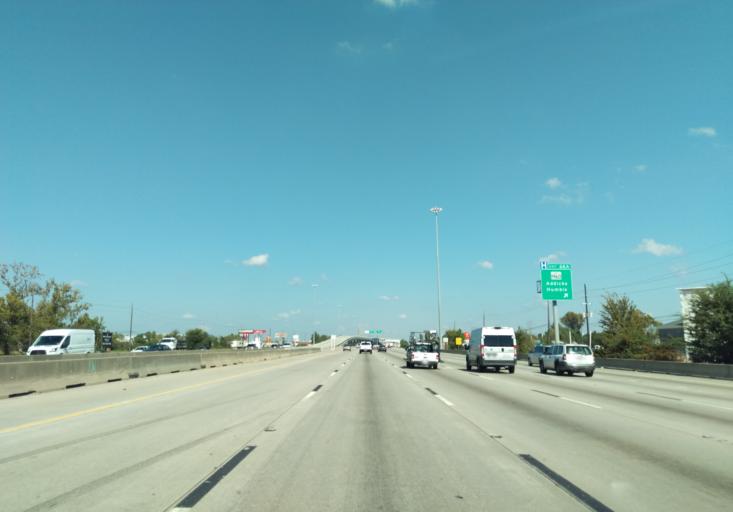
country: US
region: Texas
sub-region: Harris County
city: Spring
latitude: 30.0066
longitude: -95.4271
